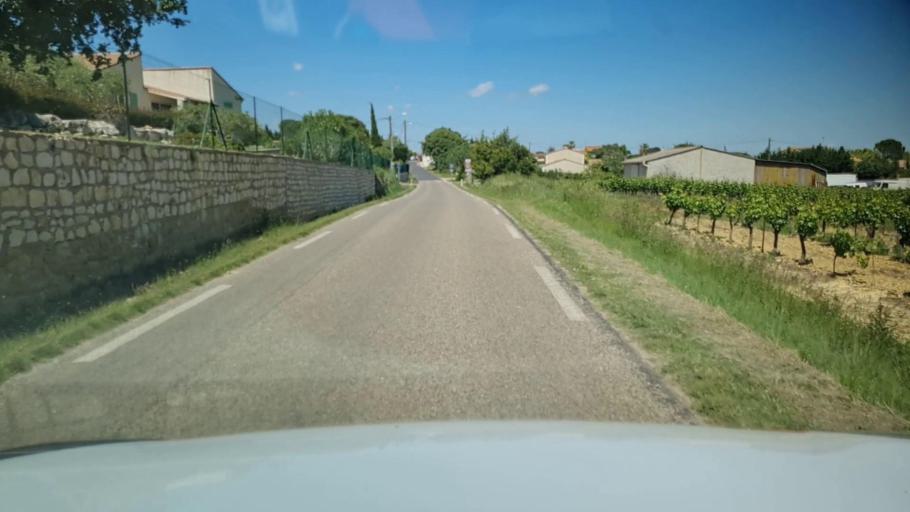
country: FR
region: Languedoc-Roussillon
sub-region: Departement du Gard
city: Saint-Mamert-du-Gard
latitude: 43.9035
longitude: 4.1923
